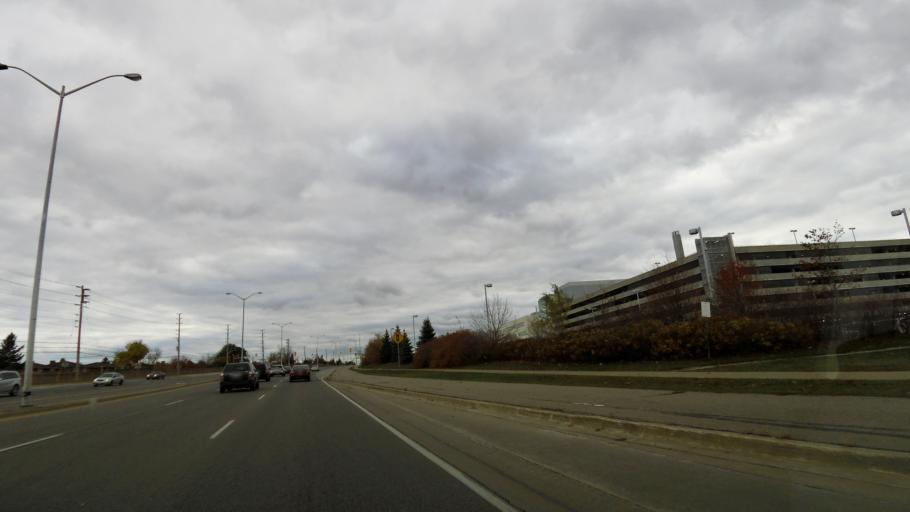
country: CA
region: Ontario
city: Brampton
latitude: 43.7488
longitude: -79.7399
